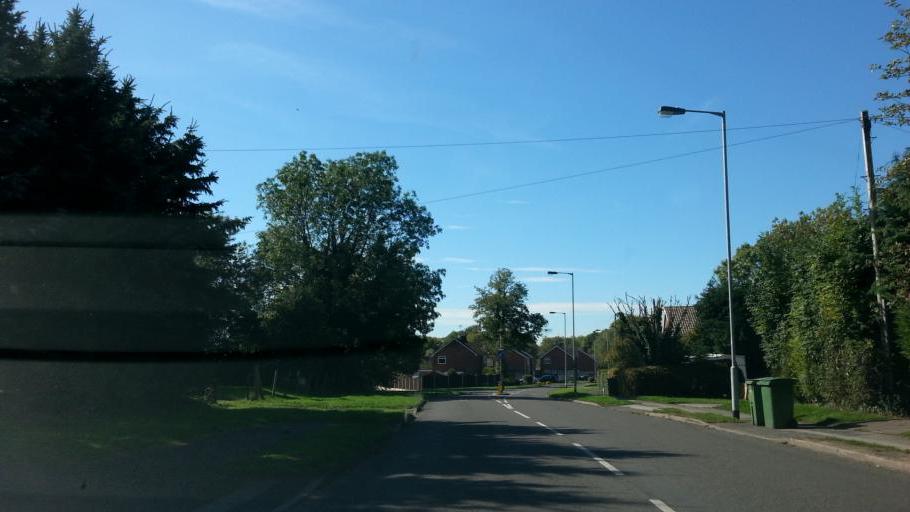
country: GB
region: England
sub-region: Staffordshire
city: Stafford
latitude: 52.8112
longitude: -2.1485
